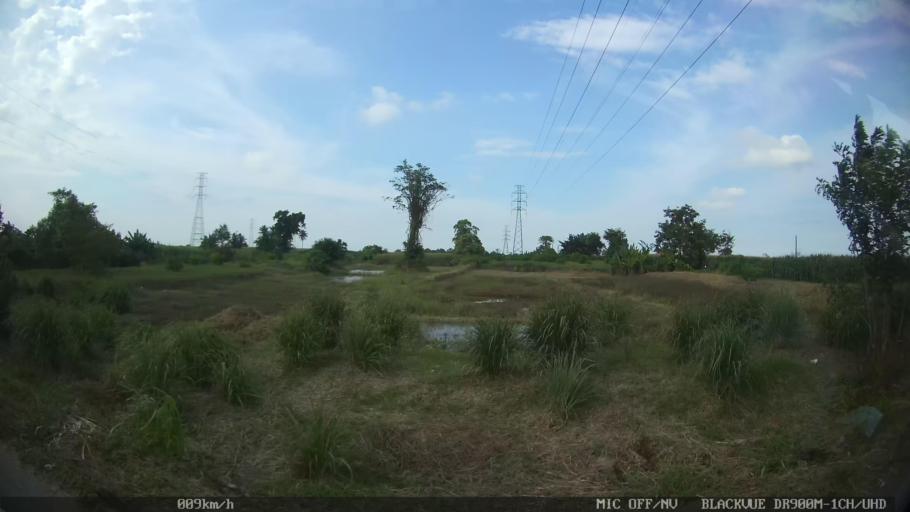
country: ID
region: North Sumatra
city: Percut
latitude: 3.5679
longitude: 98.7832
